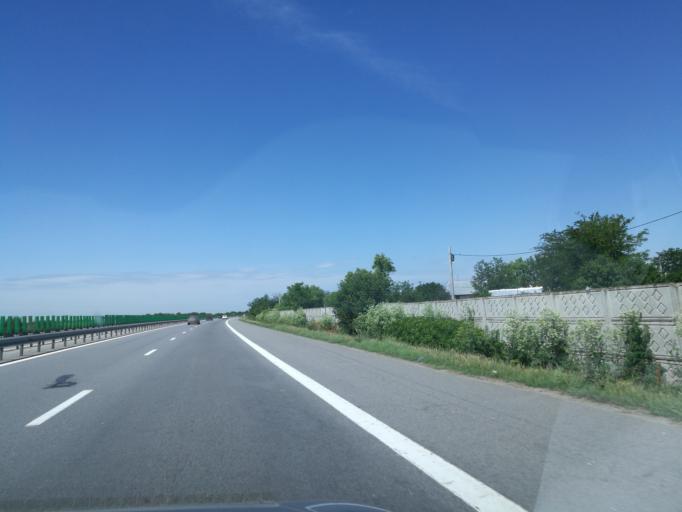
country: RO
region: Calarasi
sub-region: Comuna Sarulesti
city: Sarulesti-Gara
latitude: 44.4394
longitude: 26.6615
